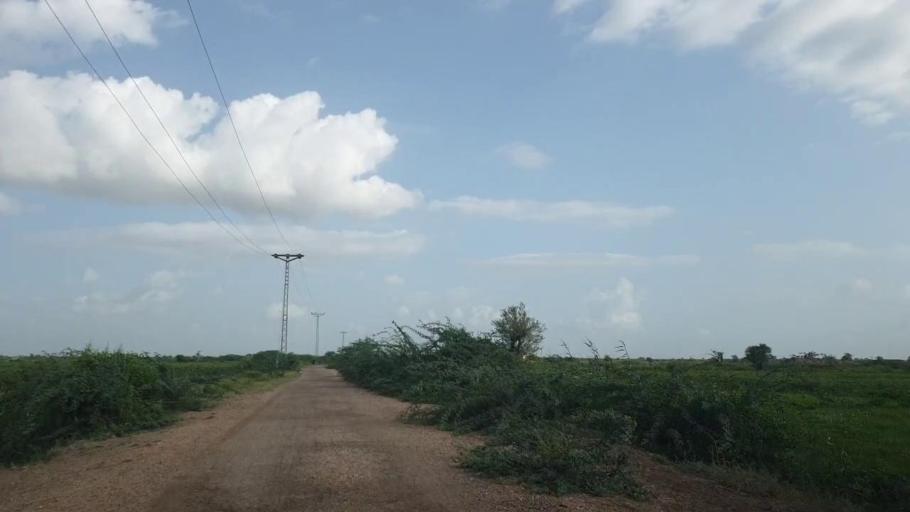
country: PK
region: Sindh
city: Kadhan
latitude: 24.6383
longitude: 69.0806
